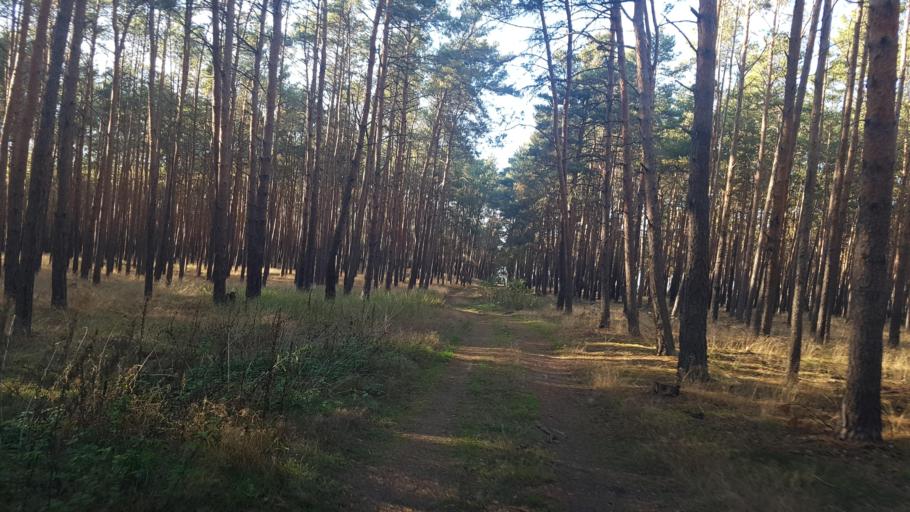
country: DE
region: Brandenburg
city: Herzberg
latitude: 51.6636
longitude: 13.3089
